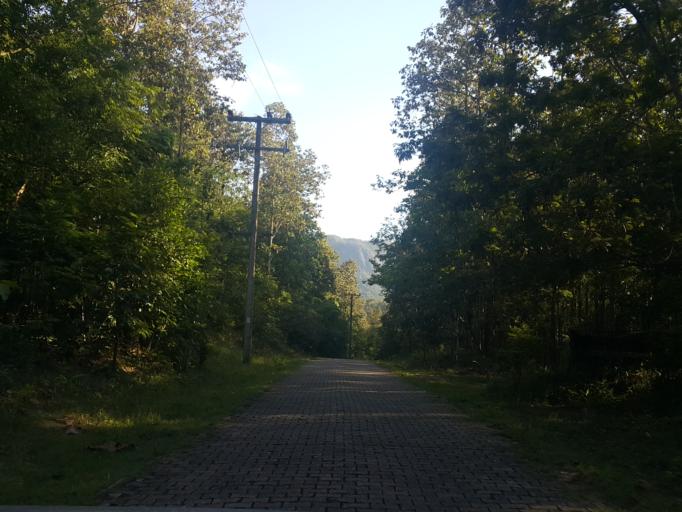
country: TH
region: Chiang Mai
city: Mae On
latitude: 18.6979
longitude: 99.2067
